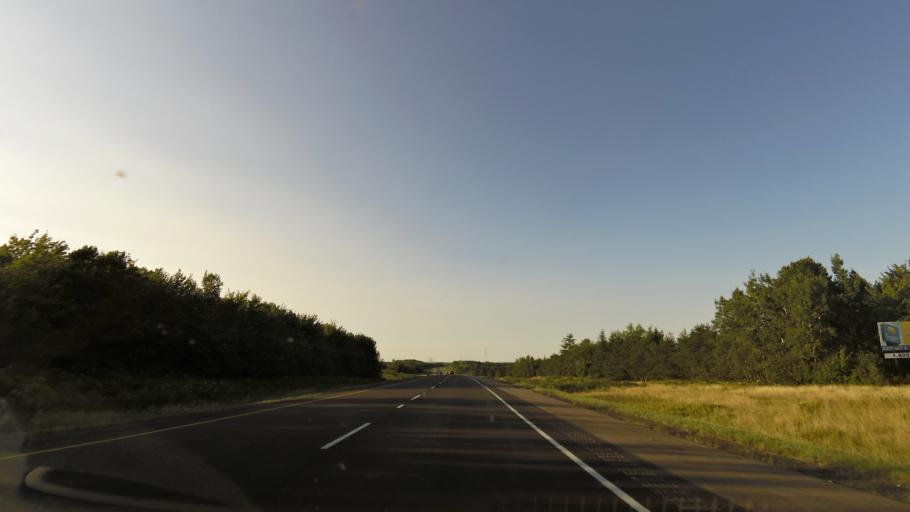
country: CA
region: New Brunswick
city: Dieppe
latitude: 46.0650
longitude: -64.5884
